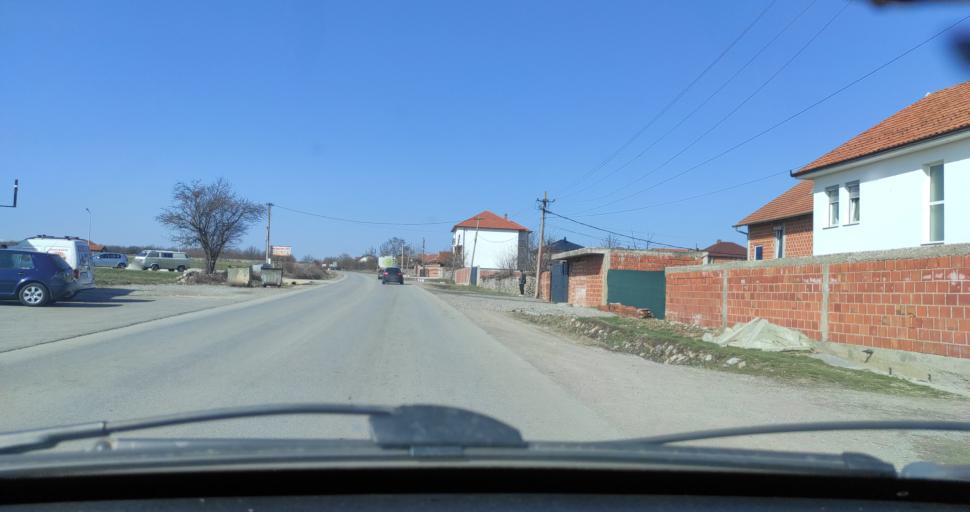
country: XK
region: Prizren
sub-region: Komuna e Malisheves
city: Llazice
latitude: 42.5852
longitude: 20.6892
